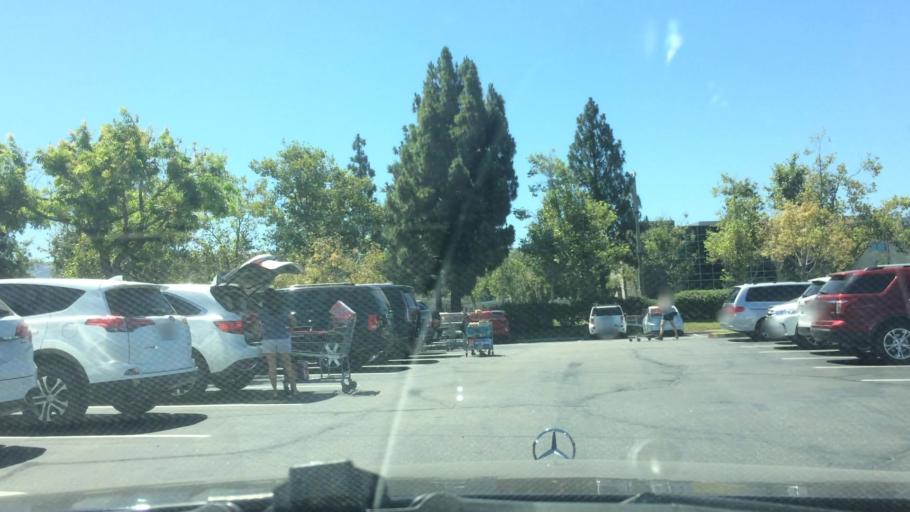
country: US
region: California
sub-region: Orange County
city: Yorba Linda
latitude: 33.8753
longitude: -117.7443
